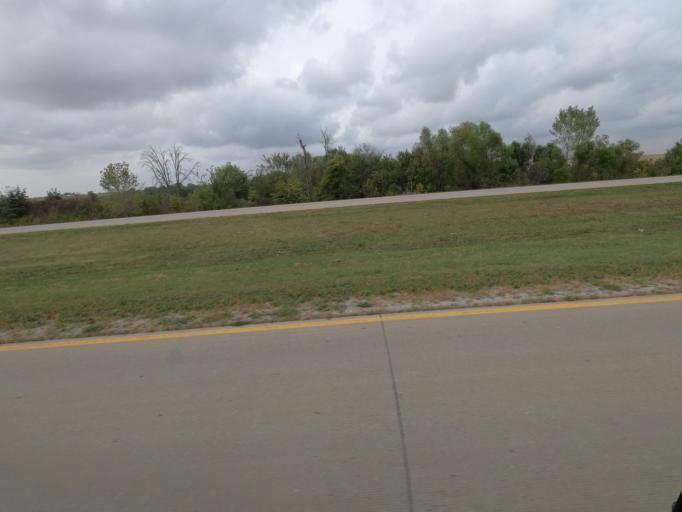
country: US
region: Iowa
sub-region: Wapello County
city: Ottumwa
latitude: 41.0017
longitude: -92.2699
